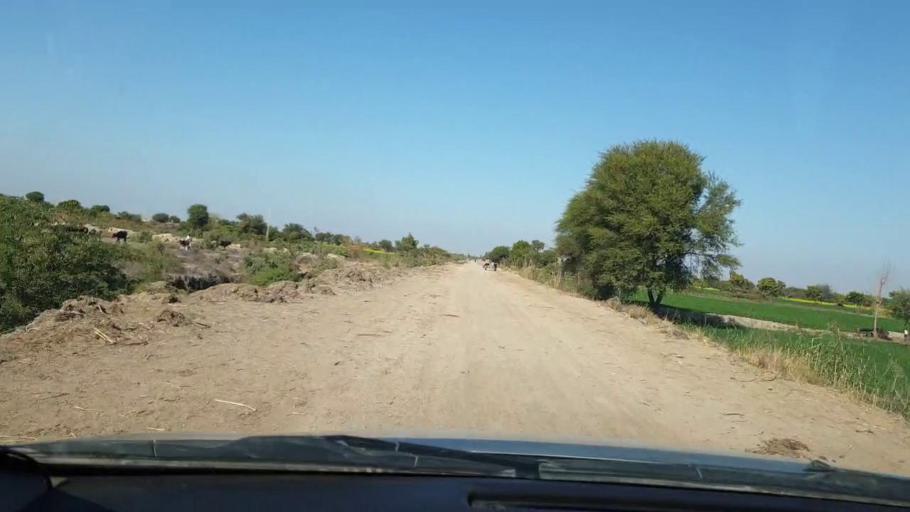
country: PK
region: Sindh
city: Berani
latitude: 25.7224
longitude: 68.9884
